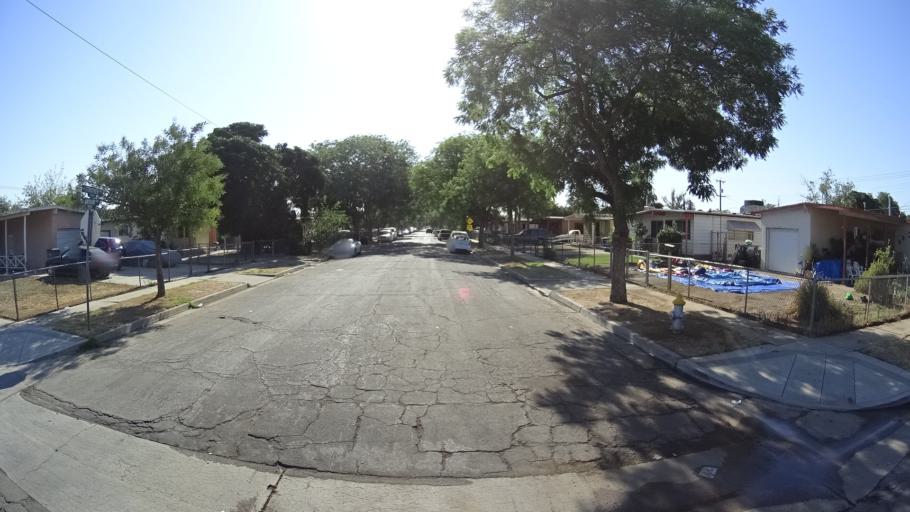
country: US
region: California
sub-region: Fresno County
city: West Park
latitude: 36.7264
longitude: -119.8154
